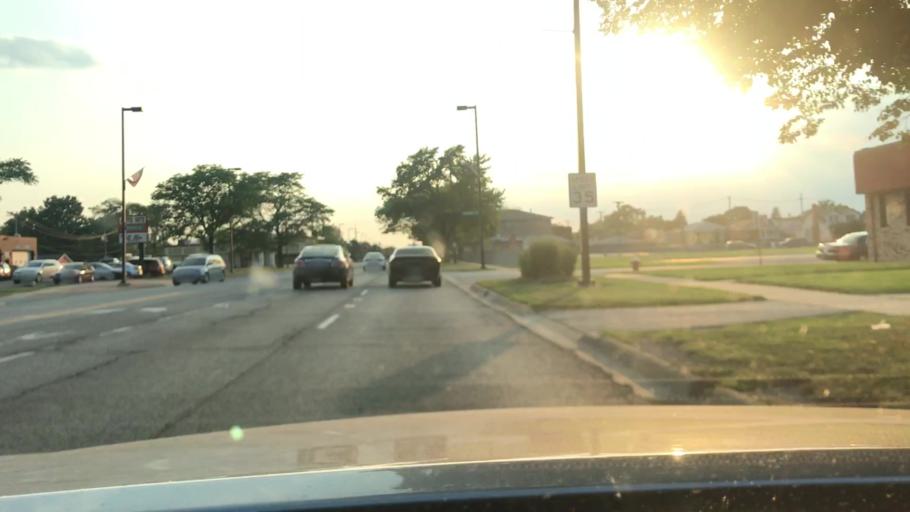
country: US
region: Illinois
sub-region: Cook County
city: Burbank
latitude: 41.7486
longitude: -87.7762
